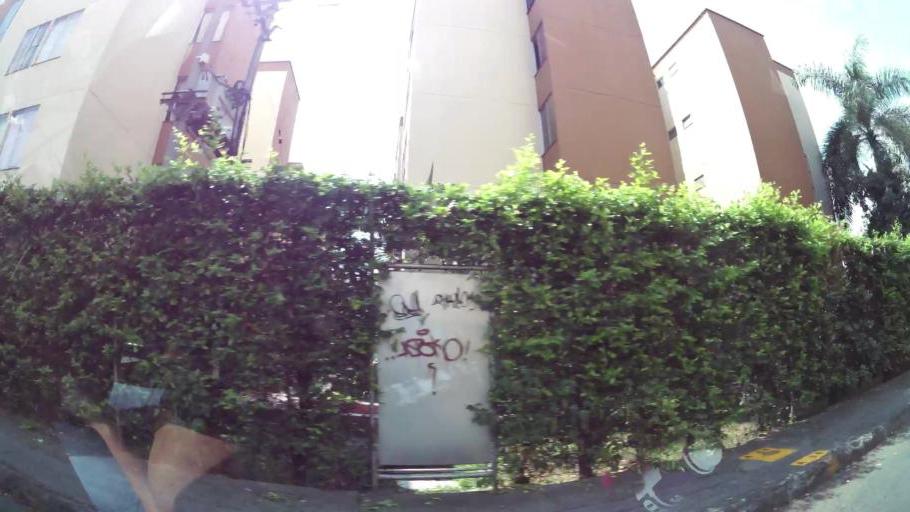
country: CO
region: Valle del Cauca
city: Cali
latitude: 3.4938
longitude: -76.5048
